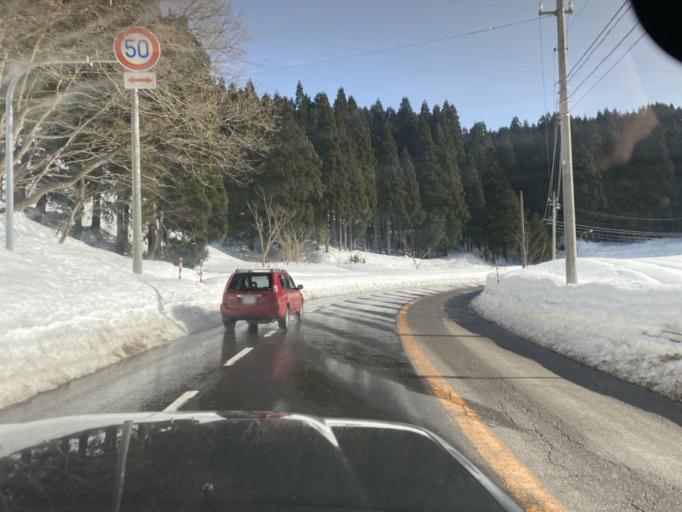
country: JP
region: Toyama
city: Fukumitsu
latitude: 36.4693
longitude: 136.8981
